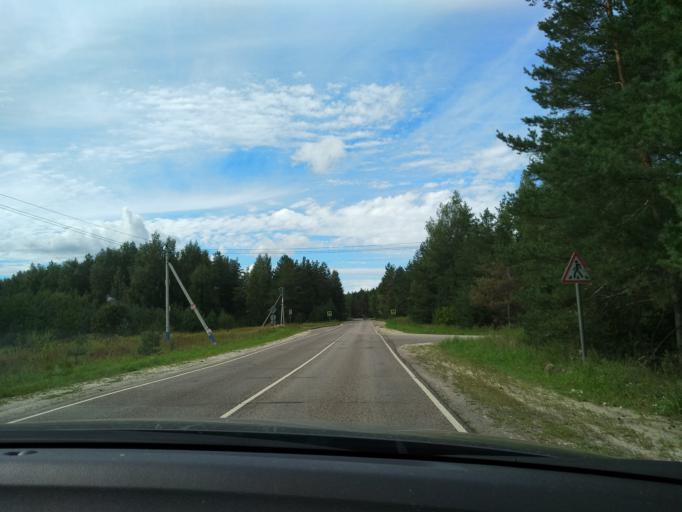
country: RU
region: Moskovskaya
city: Krasnyy Tkach
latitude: 55.3973
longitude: 39.1345
